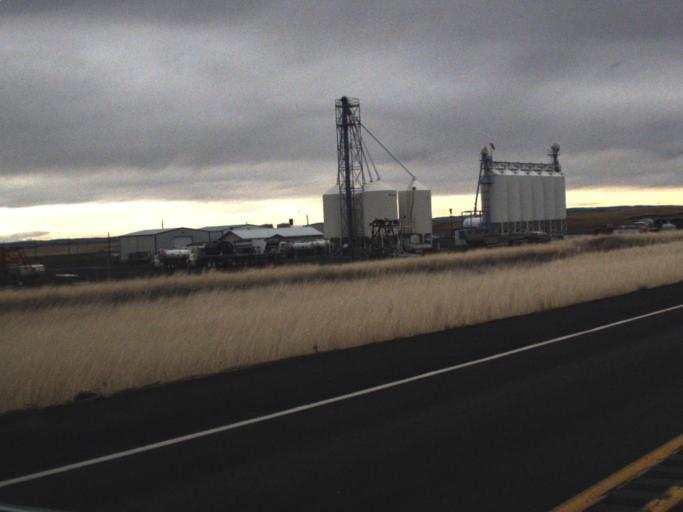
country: US
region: Washington
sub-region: Walla Walla County
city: Walla Walla East
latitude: 46.0922
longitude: -118.2569
